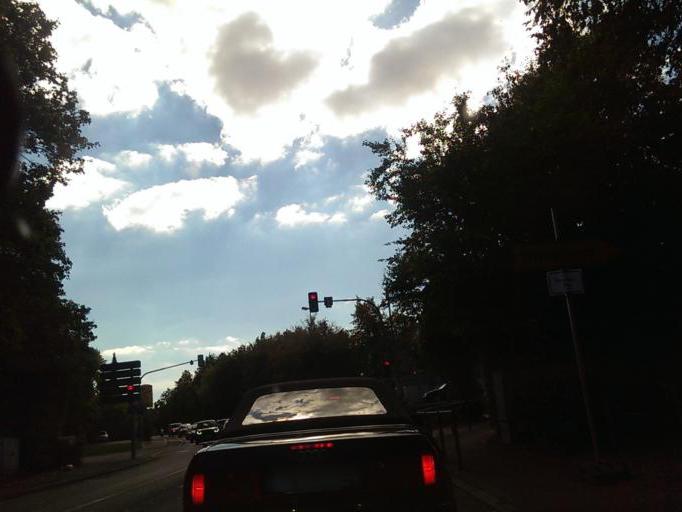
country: DE
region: Baden-Wuerttemberg
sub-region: Regierungsbezirk Stuttgart
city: Boeblingen
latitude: 48.6797
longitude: 9.0107
